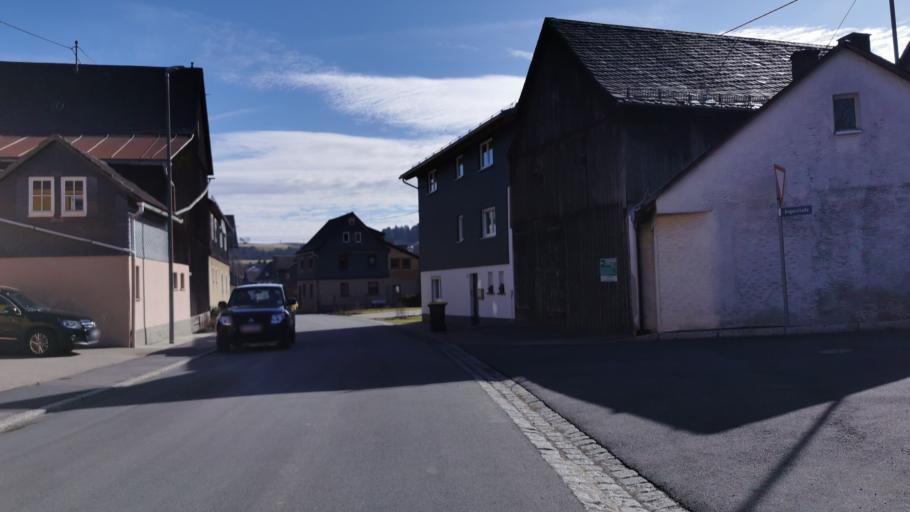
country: DE
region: Bavaria
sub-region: Upper Franconia
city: Ludwigsstadt
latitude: 50.4899
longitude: 11.3459
